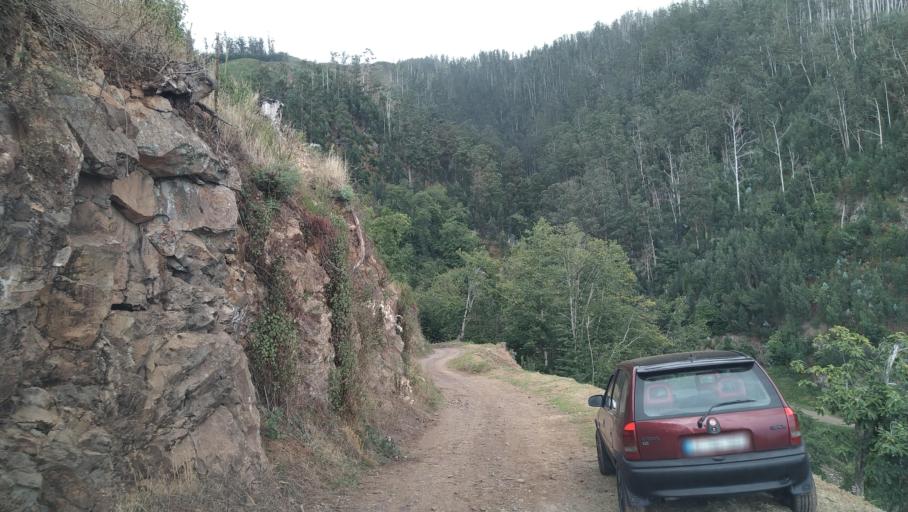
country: PT
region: Madeira
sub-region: Funchal
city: Nossa Senhora do Monte
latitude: 32.6829
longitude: -16.9265
